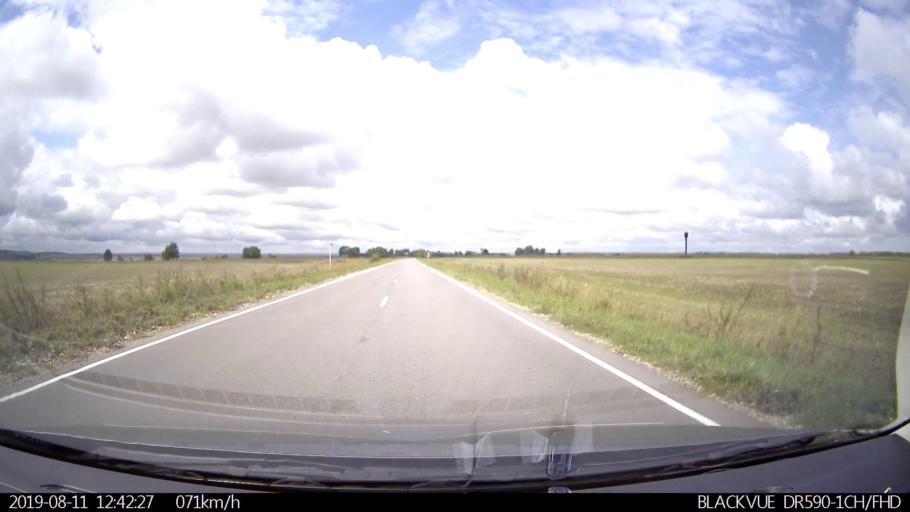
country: RU
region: Ulyanovsk
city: Ignatovka
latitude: 53.8460
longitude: 47.7513
